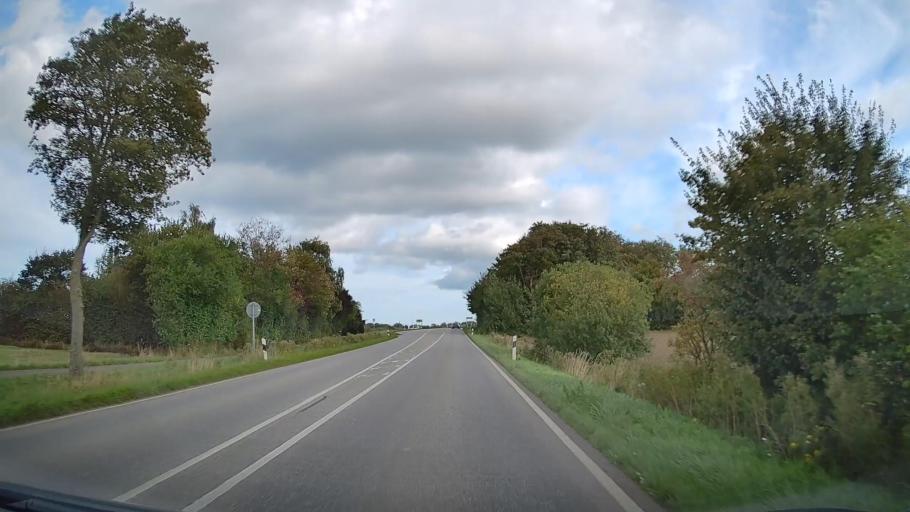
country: DE
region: Schleswig-Holstein
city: Niesgrau
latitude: 54.7509
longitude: 9.8181
